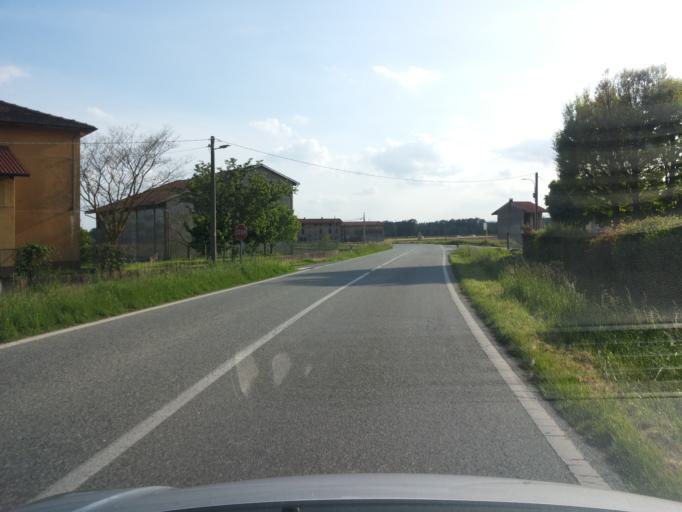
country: IT
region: Piedmont
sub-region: Provincia di Torino
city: Bollengo
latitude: 45.4667
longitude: 7.9480
